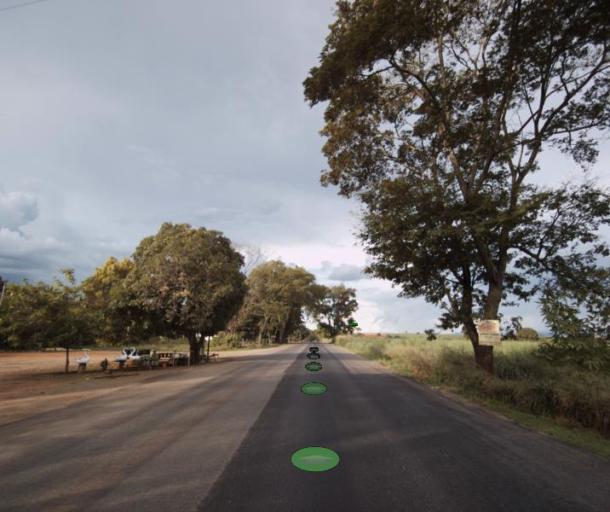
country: BR
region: Goias
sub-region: Itapaci
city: Itapaci
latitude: -15.1209
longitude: -49.5008
